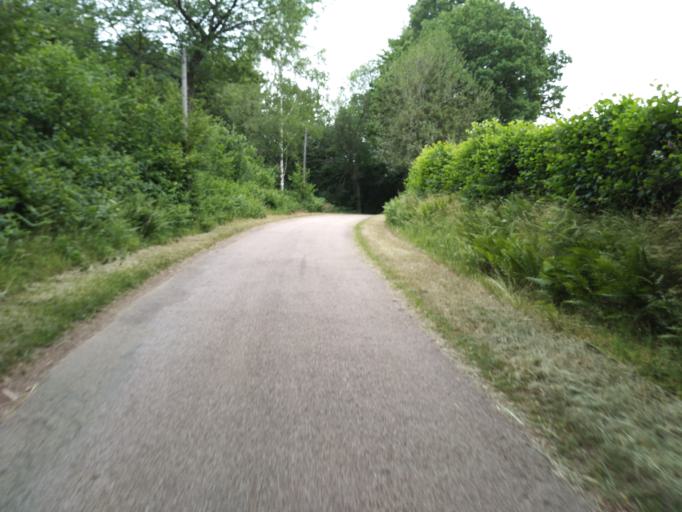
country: FR
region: Bourgogne
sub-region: Departement de la Cote-d'Or
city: Saulieu
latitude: 47.2768
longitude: 4.1242
